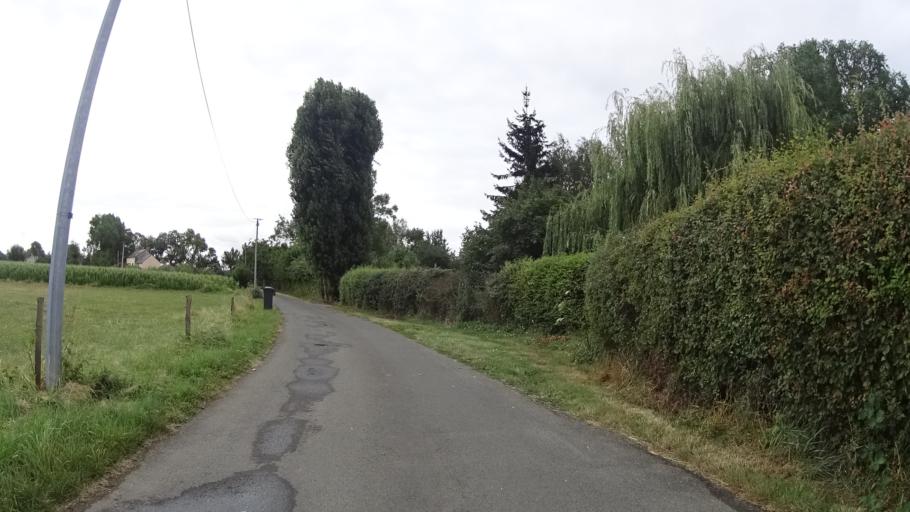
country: FR
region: Pays de la Loire
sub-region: Departement de Maine-et-Loire
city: Montjean-sur-Loire
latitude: 47.3856
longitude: -0.8393
